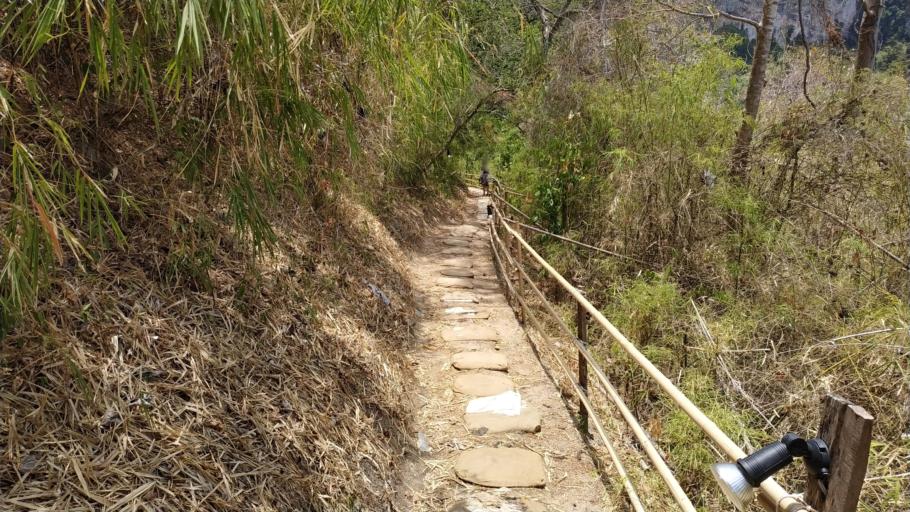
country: TH
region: Phangnga
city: Ban Ao Nang
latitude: 8.0254
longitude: 98.8275
